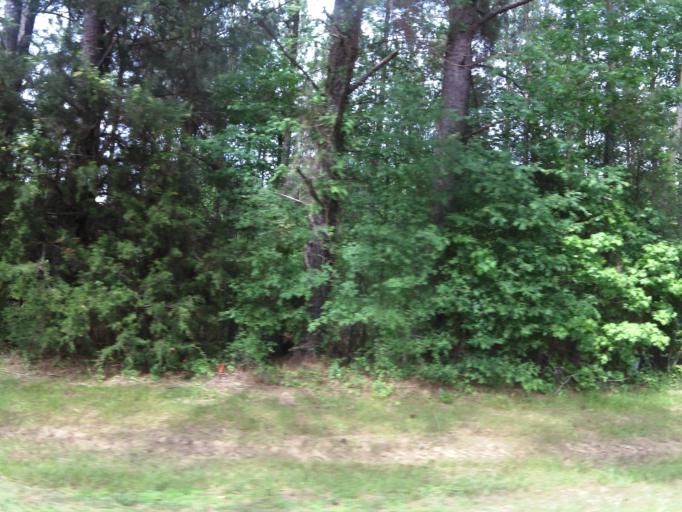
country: US
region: Georgia
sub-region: McDuffie County
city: Thomson
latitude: 33.5352
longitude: -82.4943
